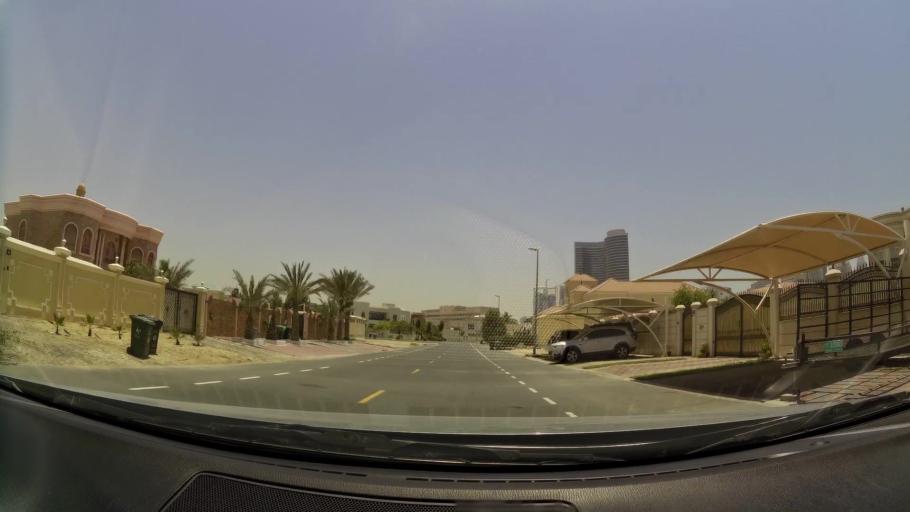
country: AE
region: Dubai
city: Dubai
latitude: 25.1000
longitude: 55.1860
